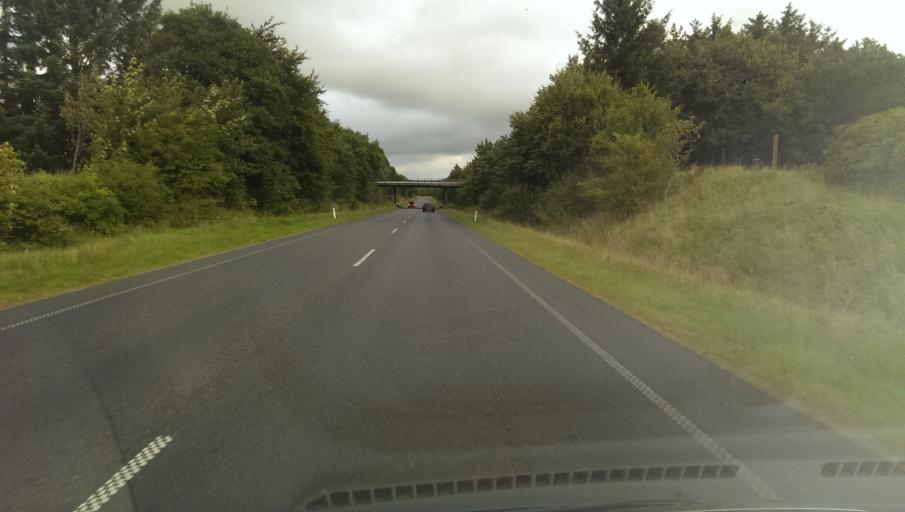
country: DK
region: South Denmark
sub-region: Varde Kommune
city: Varde
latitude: 55.6704
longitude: 8.5717
